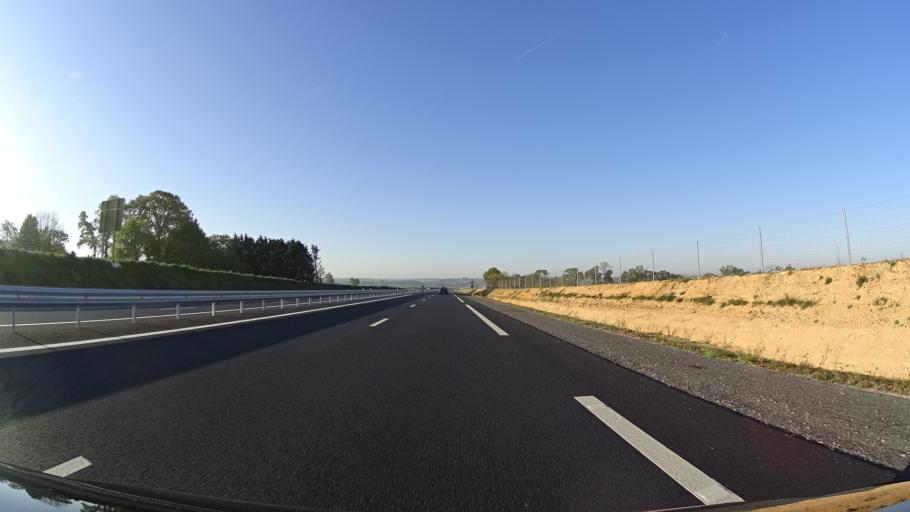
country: FR
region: Brittany
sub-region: Departement d'Ille-et-Vilaine
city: Pipriac
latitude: 47.8111
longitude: -1.9207
